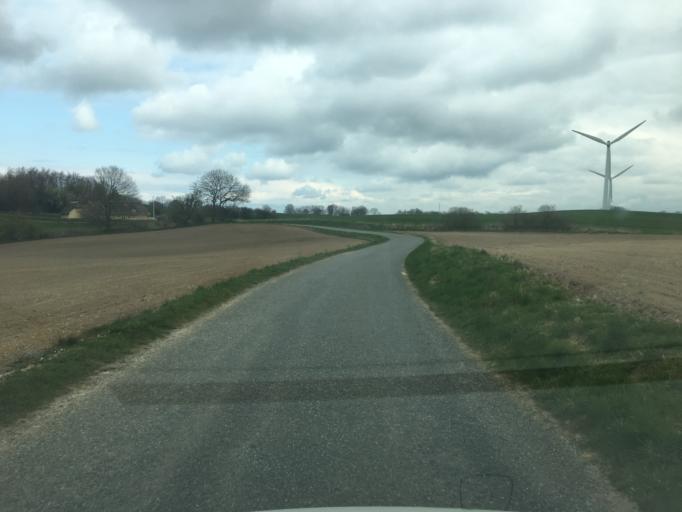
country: DK
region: South Denmark
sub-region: Sonderborg Kommune
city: Grasten
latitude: 54.9867
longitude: 9.5215
